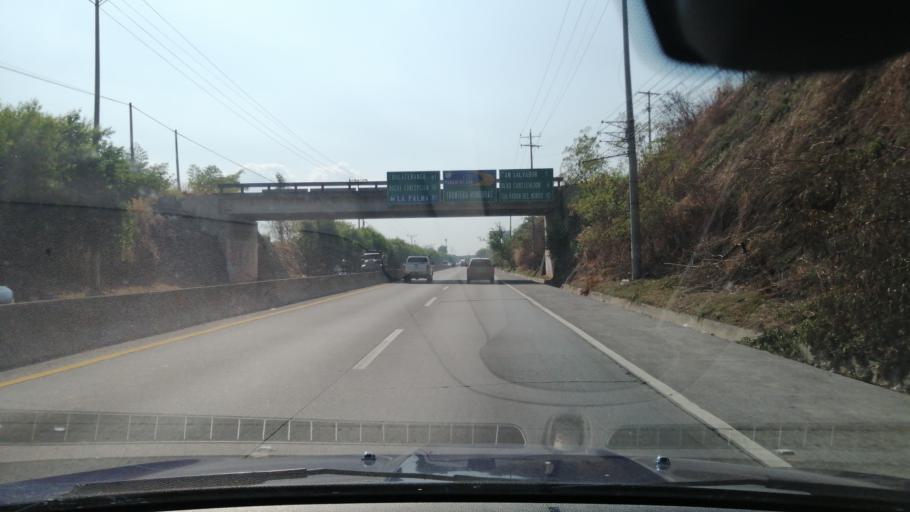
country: SV
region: San Salvador
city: Ayutuxtepeque
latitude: 13.7873
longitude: -89.2182
